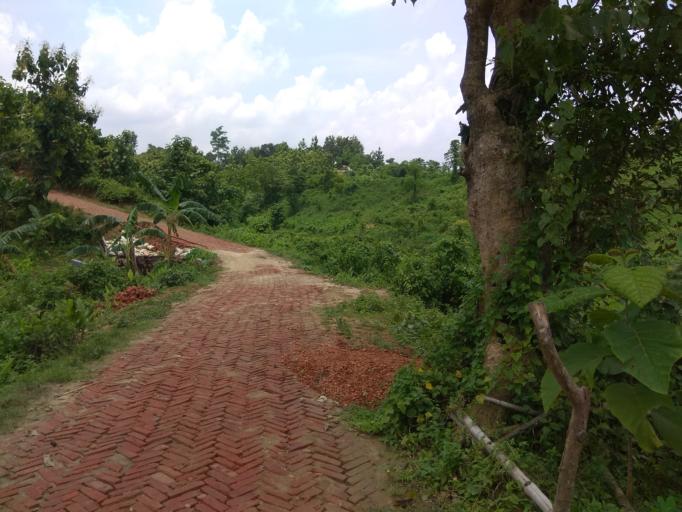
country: BD
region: Chittagong
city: Manikchari
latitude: 22.8857
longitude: 91.9243
